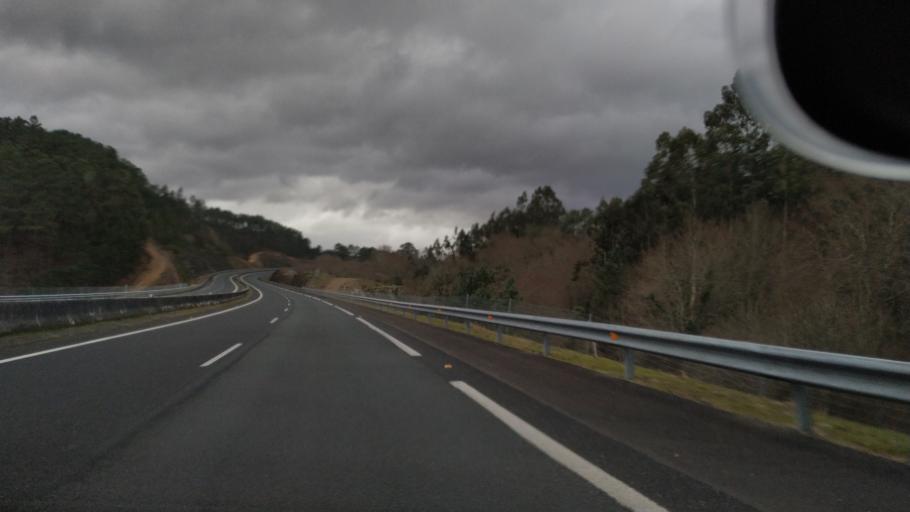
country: ES
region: Galicia
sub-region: Provincia da Coruna
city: Vedra
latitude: 42.7924
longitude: -8.4803
